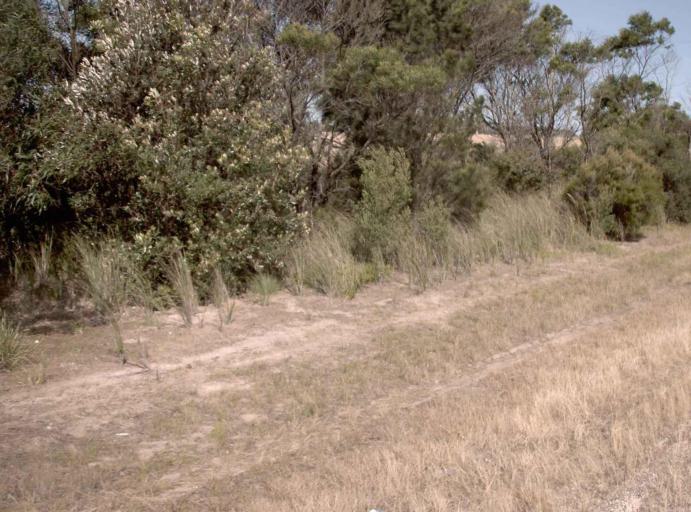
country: AU
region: Victoria
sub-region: Wellington
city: Sale
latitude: -38.3391
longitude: 147.1649
